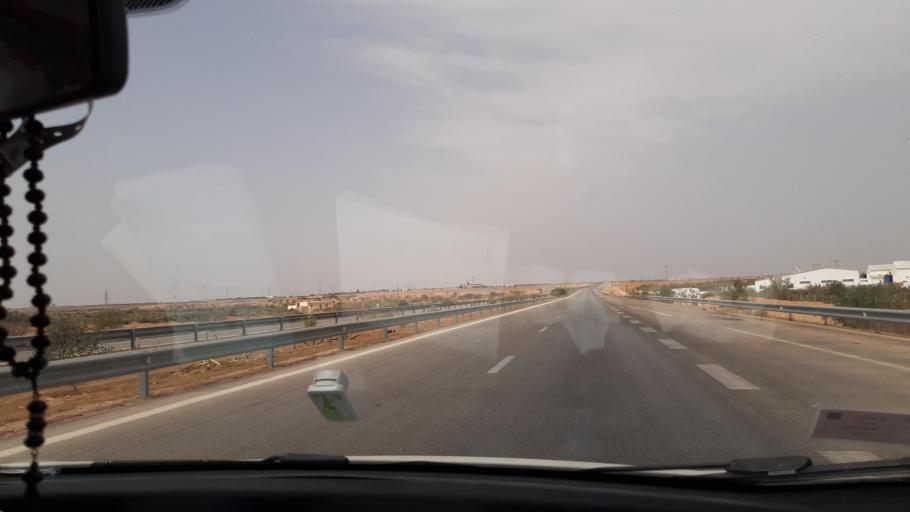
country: TN
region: Safaqis
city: Sfax
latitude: 34.7756
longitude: 10.6118
